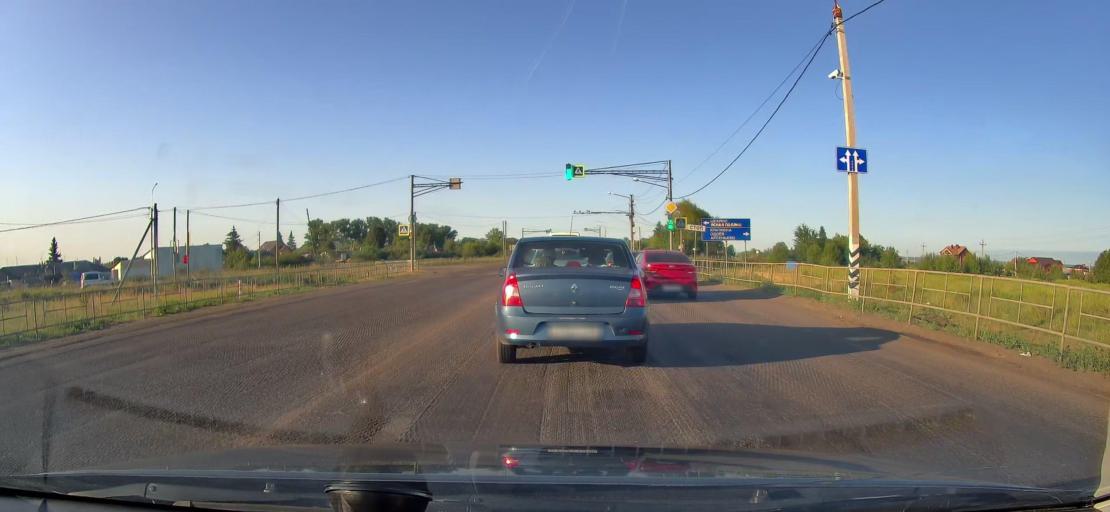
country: RU
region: Tula
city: Shchekino
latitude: 53.9975
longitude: 37.4739
